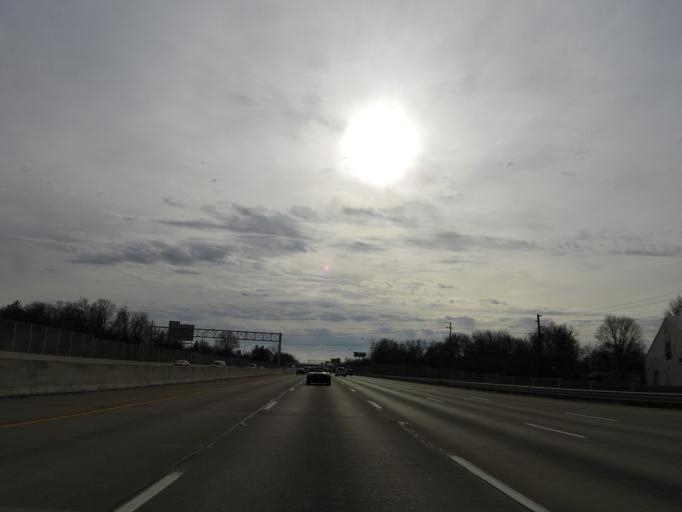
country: US
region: Indiana
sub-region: Marion County
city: Lawrence
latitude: 39.8452
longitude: -86.0433
